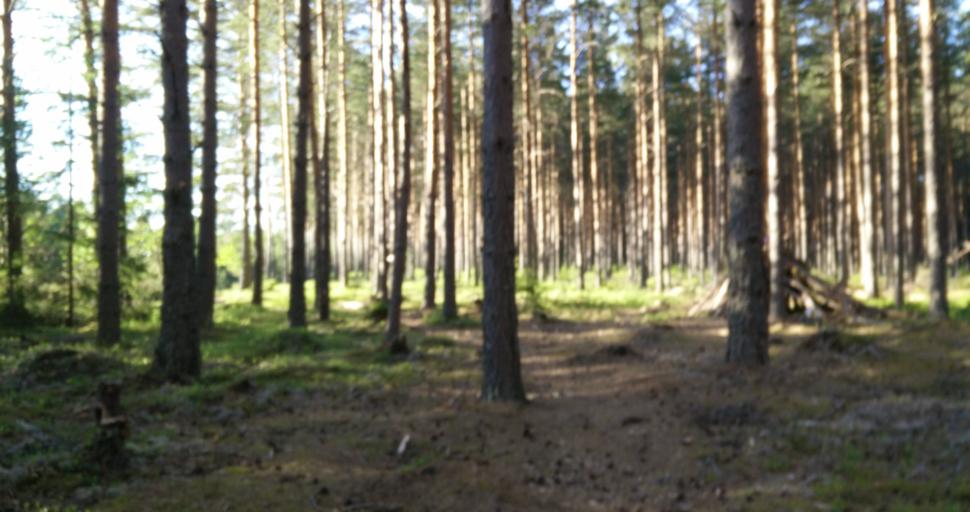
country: SE
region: Vaermland
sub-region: Hagfors Kommun
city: Hagfors
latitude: 60.0166
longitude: 13.5836
